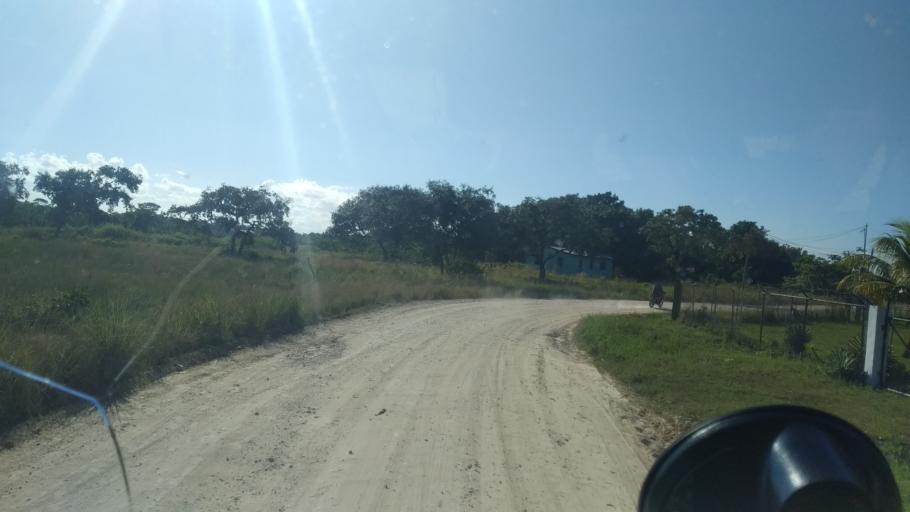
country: BZ
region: Belize
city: Belize City
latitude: 17.5546
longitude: -88.3260
